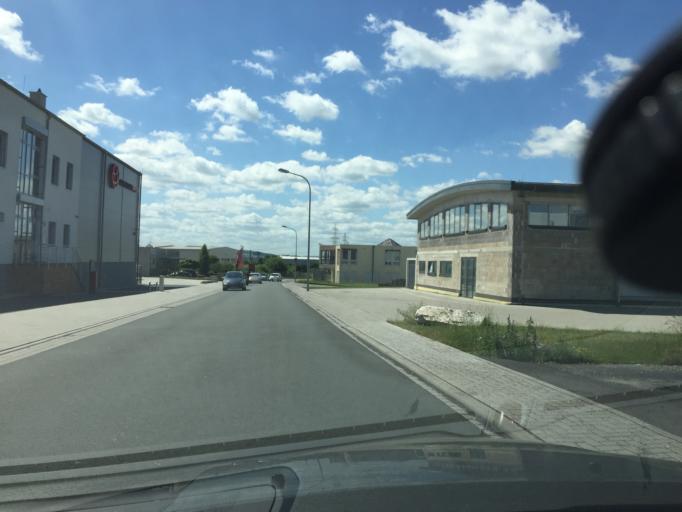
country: DE
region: Hesse
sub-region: Regierungsbezirk Giessen
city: Dehrn
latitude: 50.4074
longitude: 8.0780
